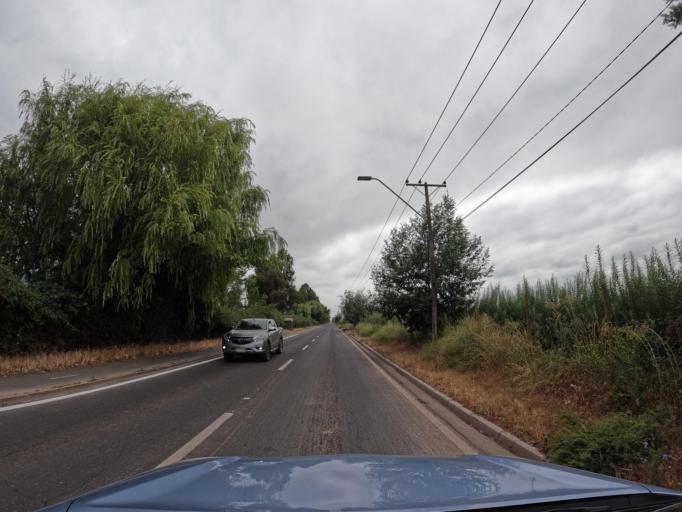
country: CL
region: O'Higgins
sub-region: Provincia de Colchagua
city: Chimbarongo
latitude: -34.7295
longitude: -71.0592
